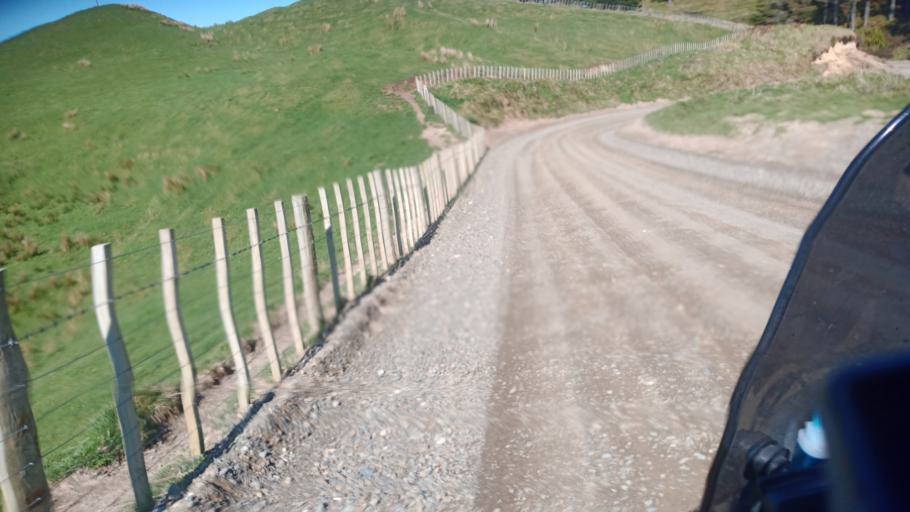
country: NZ
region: Gisborne
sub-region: Gisborne District
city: Gisborne
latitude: -39.1716
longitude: 177.9018
